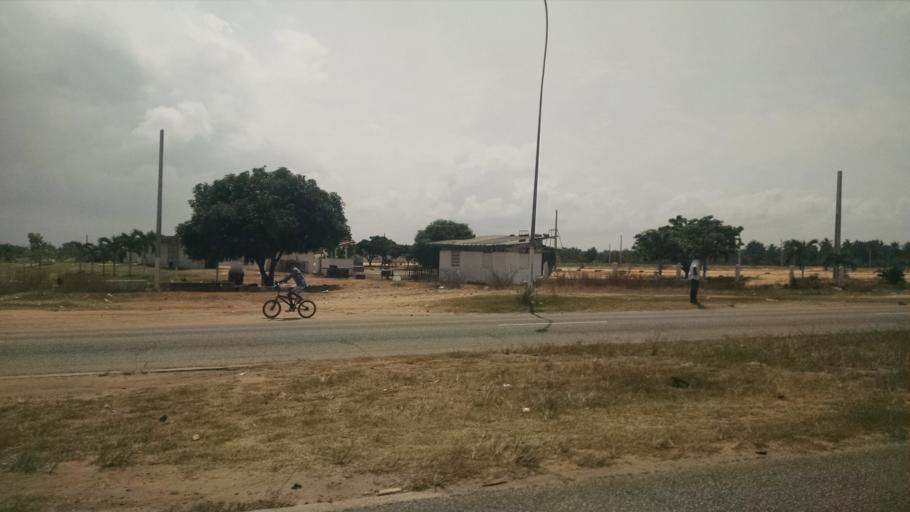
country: CI
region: Lagunes
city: Abidjan
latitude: 5.2627
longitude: -3.9484
